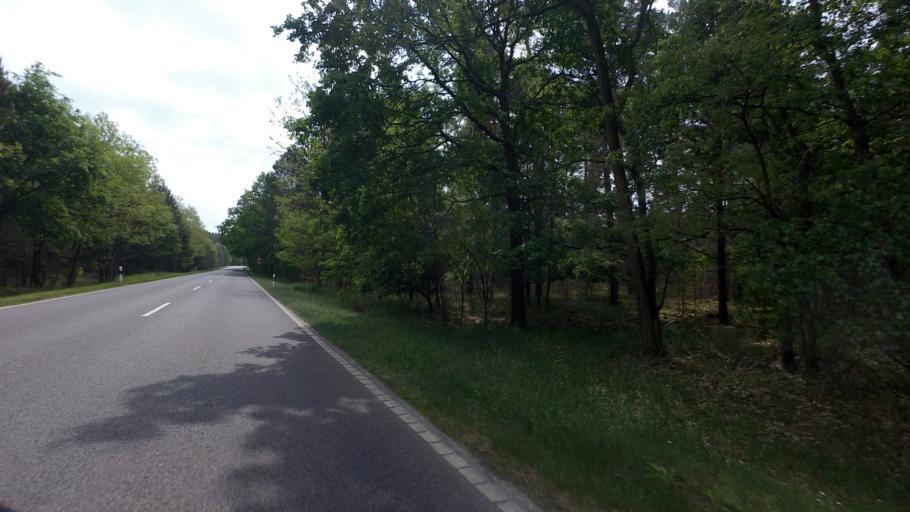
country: DE
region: Brandenburg
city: Lieberose
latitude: 51.9574
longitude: 14.3271
